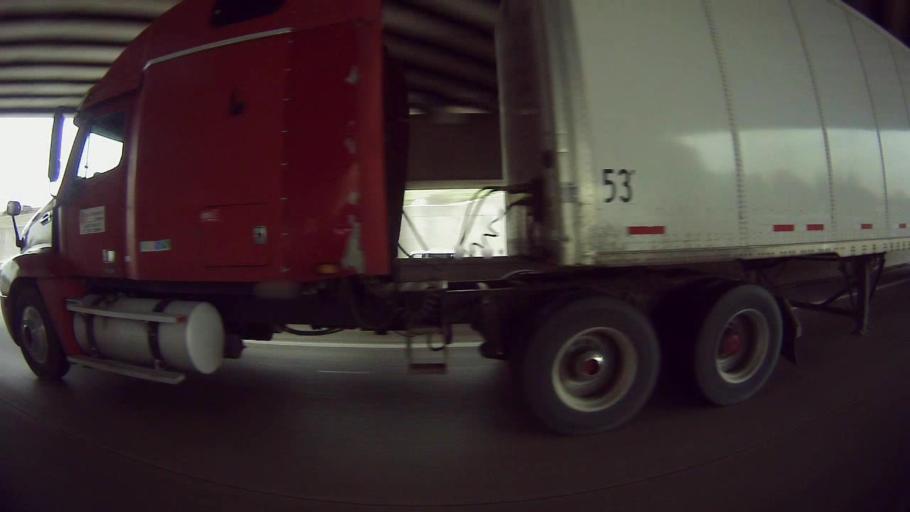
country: US
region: Michigan
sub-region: Wayne County
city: Dearborn Heights
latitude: 42.3791
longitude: -83.2348
